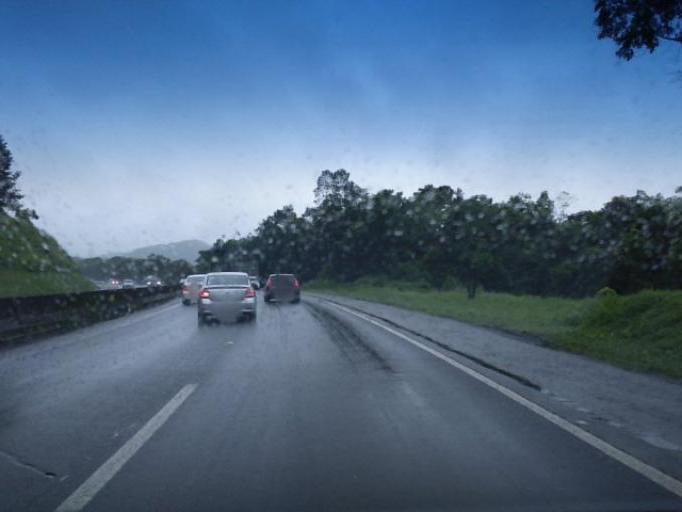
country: BR
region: Santa Catarina
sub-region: Joinville
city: Joinville
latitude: -26.1298
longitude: -48.8900
